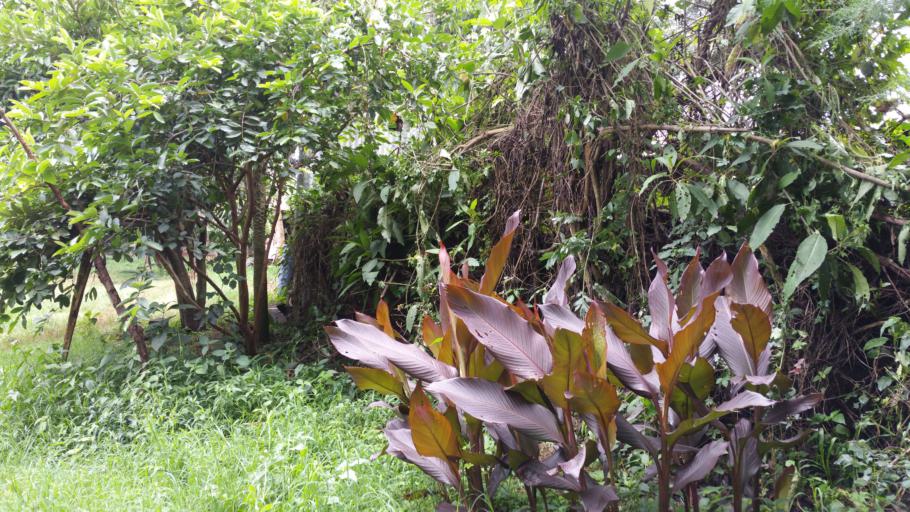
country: ET
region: Amhara
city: Bahir Dar
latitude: 11.6899
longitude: 37.3525
